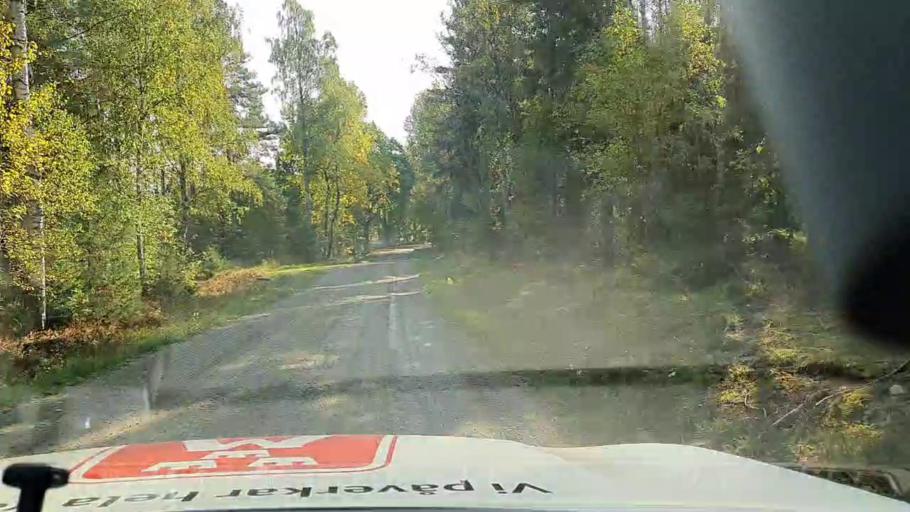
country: SE
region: Soedermanland
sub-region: Eskilstuna Kommun
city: Kvicksund
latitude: 59.3273
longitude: 16.2334
